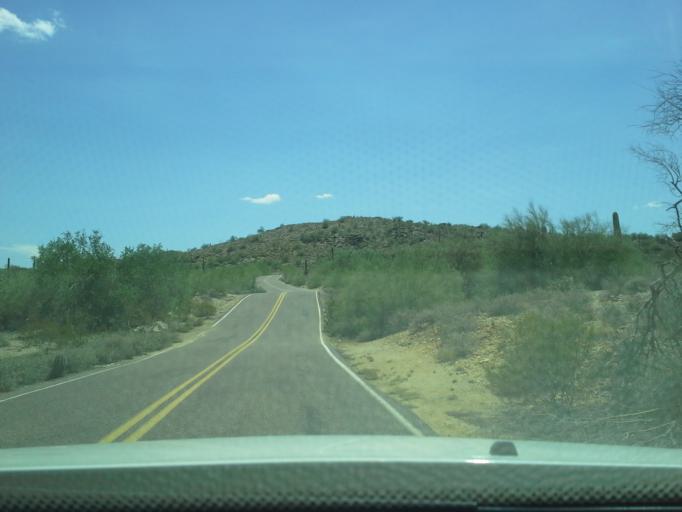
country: US
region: Arizona
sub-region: Maricopa County
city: Guadalupe
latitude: 33.3419
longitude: -112.0506
